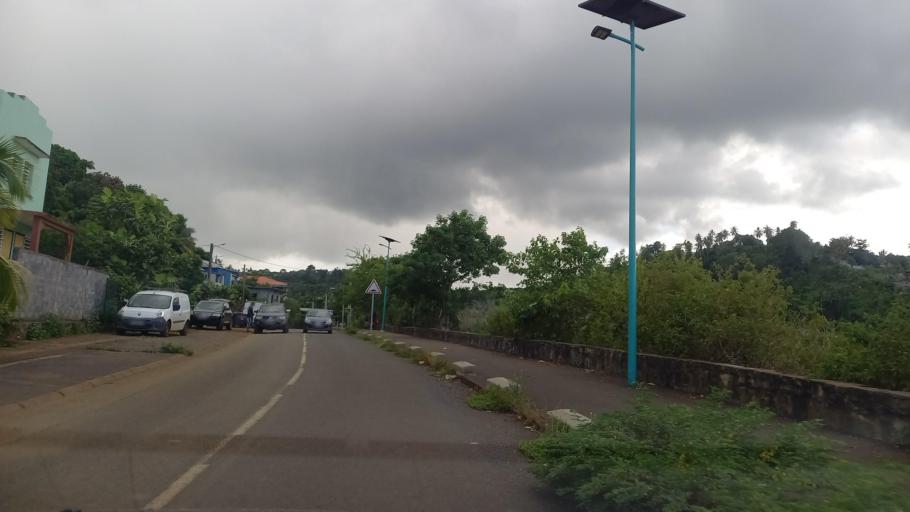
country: YT
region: Chiconi
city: Chiconi
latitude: -12.8389
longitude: 45.1156
